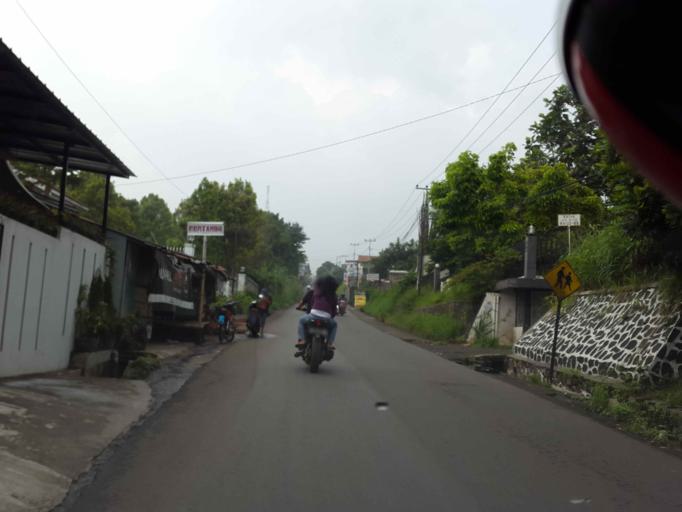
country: ID
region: West Java
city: Cimahi
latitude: -6.8546
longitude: 107.5687
